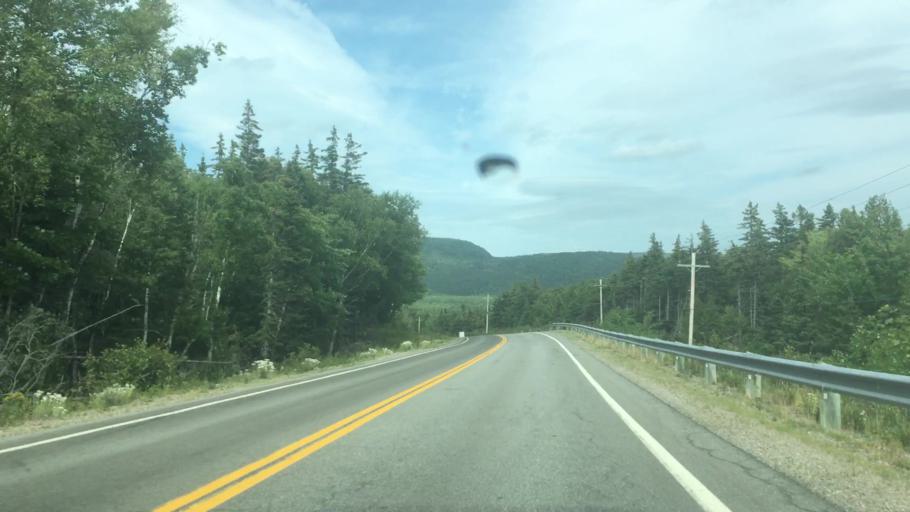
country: CA
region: Nova Scotia
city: Sydney Mines
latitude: 46.5400
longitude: -60.4141
